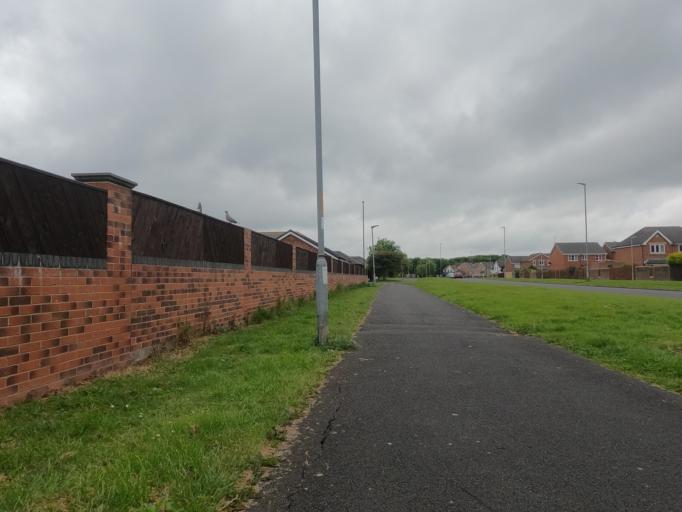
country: GB
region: England
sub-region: Northumberland
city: Blyth
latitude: 55.1089
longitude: -1.5237
